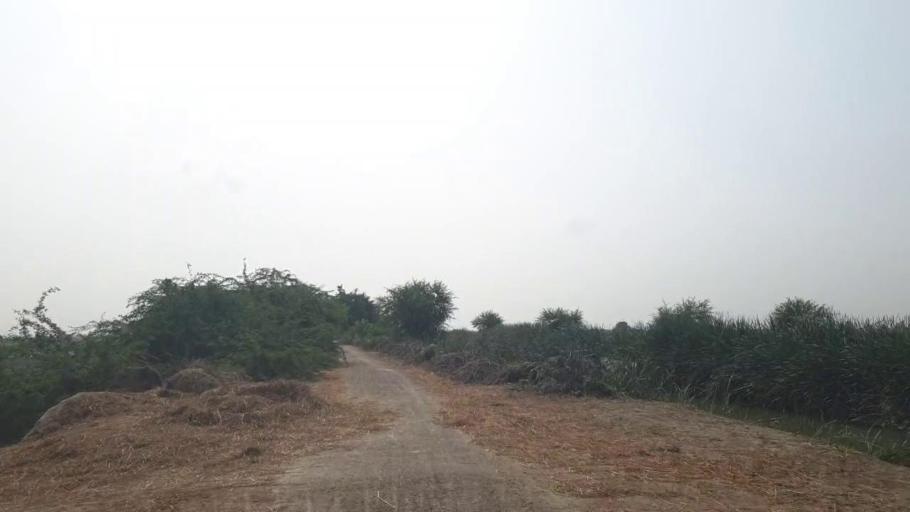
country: PK
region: Sindh
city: Badin
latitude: 24.7321
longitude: 68.7347
